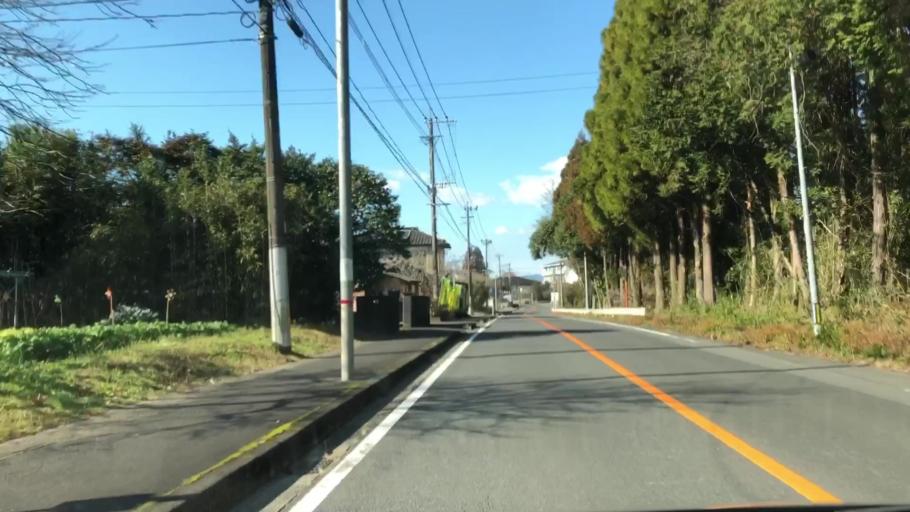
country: JP
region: Kagoshima
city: Satsumasendai
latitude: 31.7991
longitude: 130.4389
